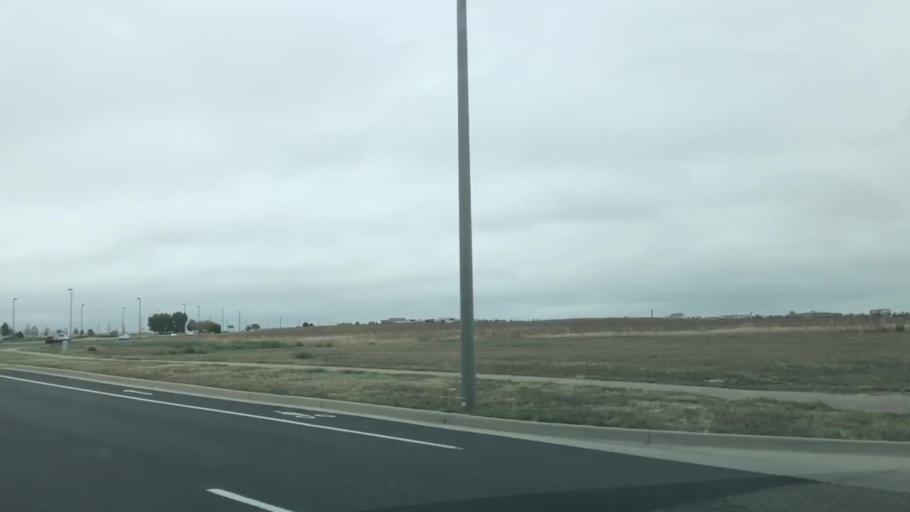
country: US
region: Colorado
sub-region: Larimer County
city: Loveland
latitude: 40.4211
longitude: -105.0007
